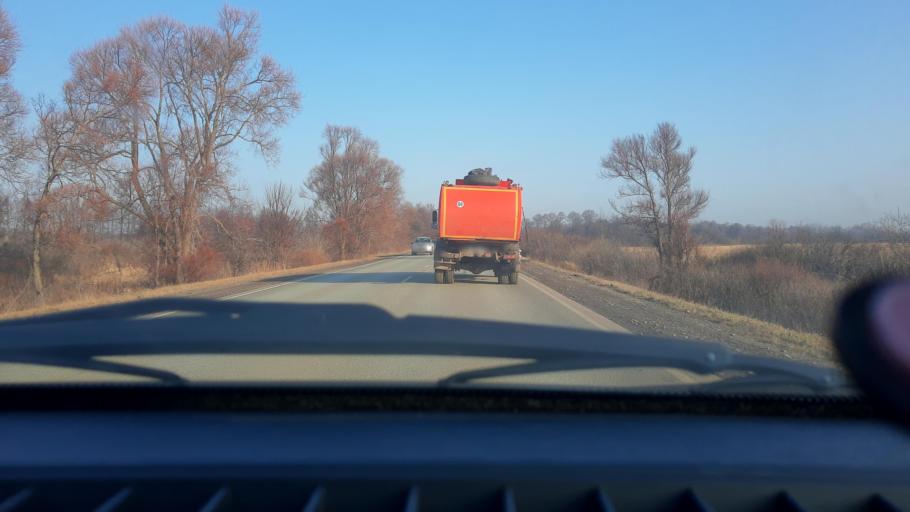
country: RU
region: Bashkortostan
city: Mikhaylovka
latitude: 54.7633
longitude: 55.8076
